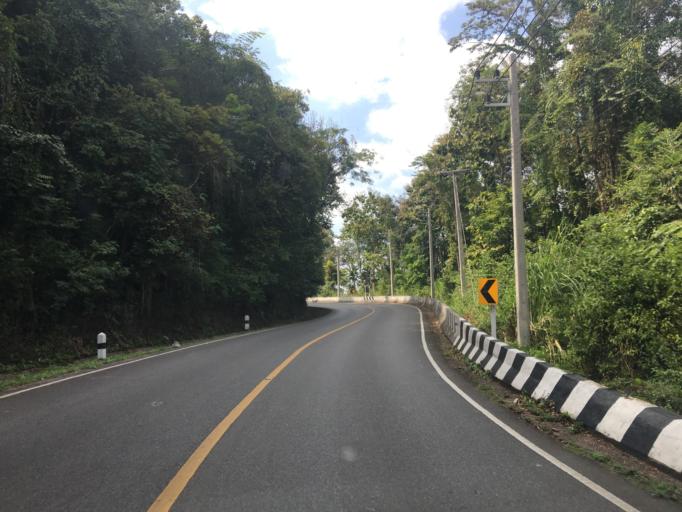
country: TH
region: Nan
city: Nan
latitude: 18.8664
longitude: 100.6247
